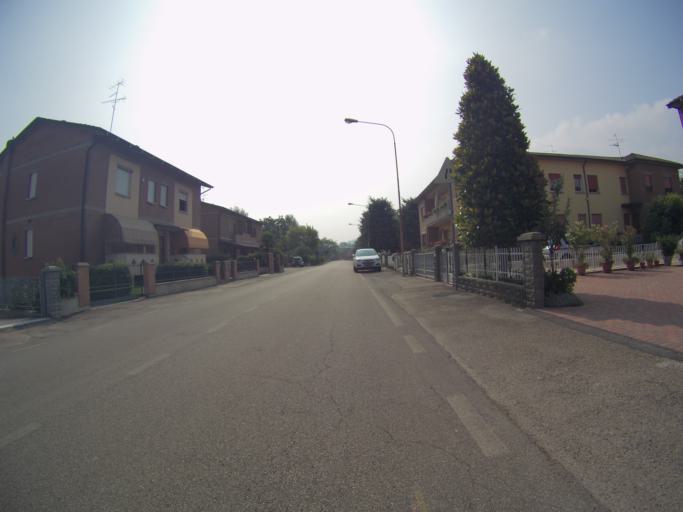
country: IT
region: Emilia-Romagna
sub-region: Provincia di Reggio Emilia
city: Pratissolo
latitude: 44.5887
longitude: 10.6704
